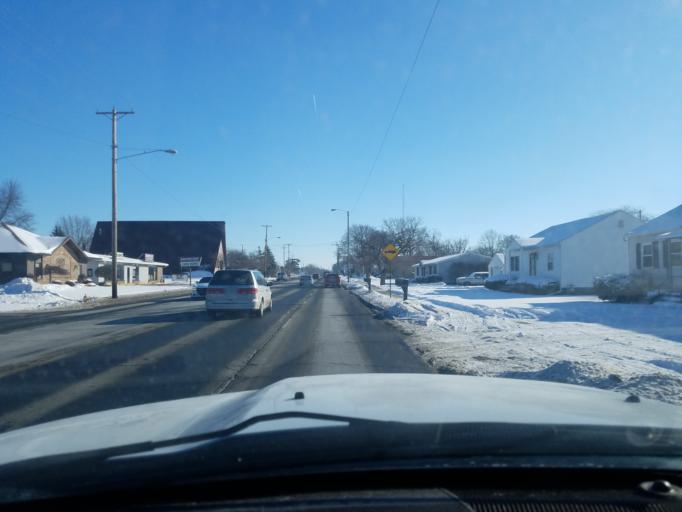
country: US
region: Indiana
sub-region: Noble County
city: Kendallville
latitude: 41.4522
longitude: -85.2650
